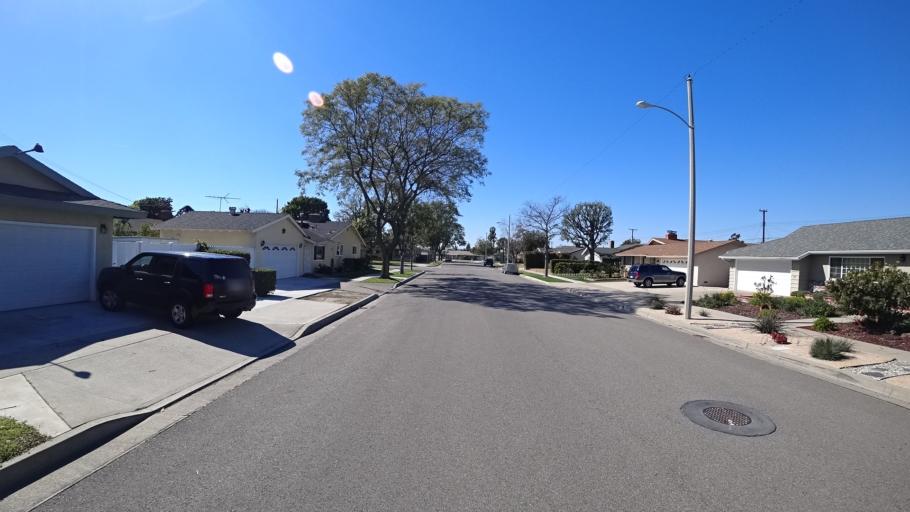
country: US
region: California
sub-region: Orange County
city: Placentia
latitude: 33.8304
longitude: -117.8728
